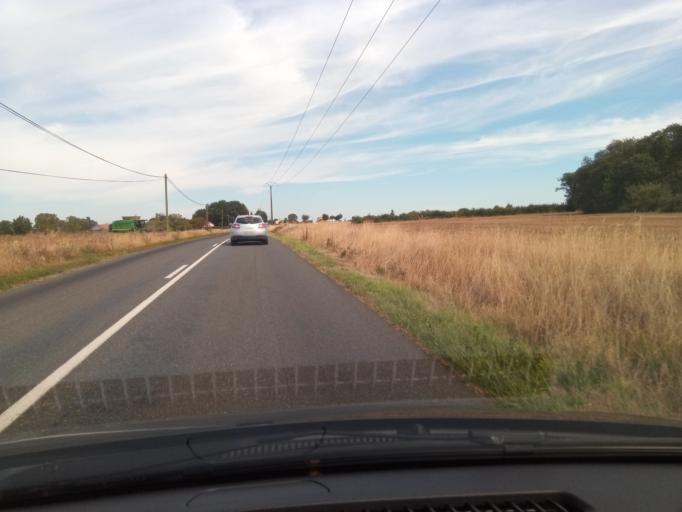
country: FR
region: Poitou-Charentes
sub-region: Departement de la Vienne
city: Terce
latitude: 46.5417
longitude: 0.5875
